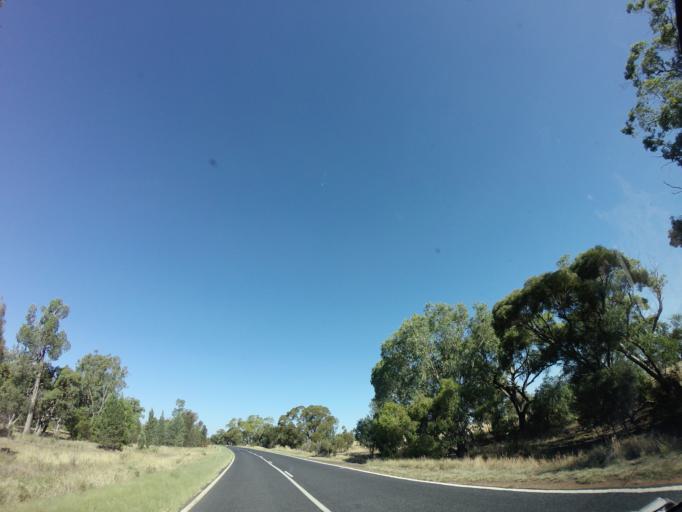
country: AU
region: New South Wales
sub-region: Gilgandra
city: Gilgandra
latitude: -31.6612
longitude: 148.3467
